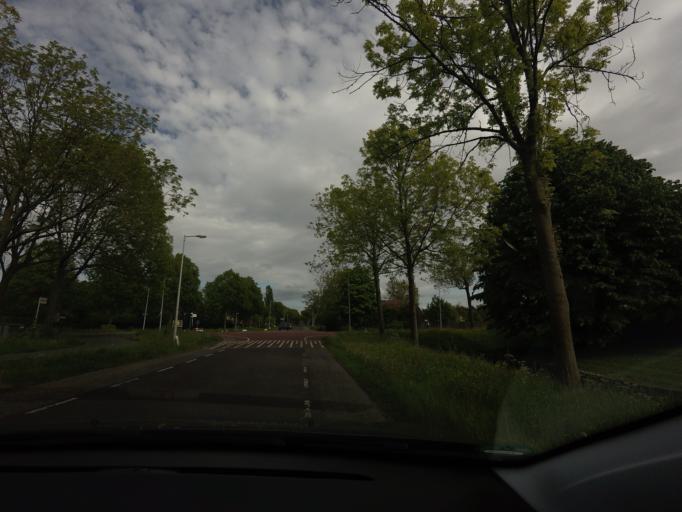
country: NL
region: North Holland
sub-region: Gemeente Beemster
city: Halfweg
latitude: 52.5178
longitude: 4.9233
